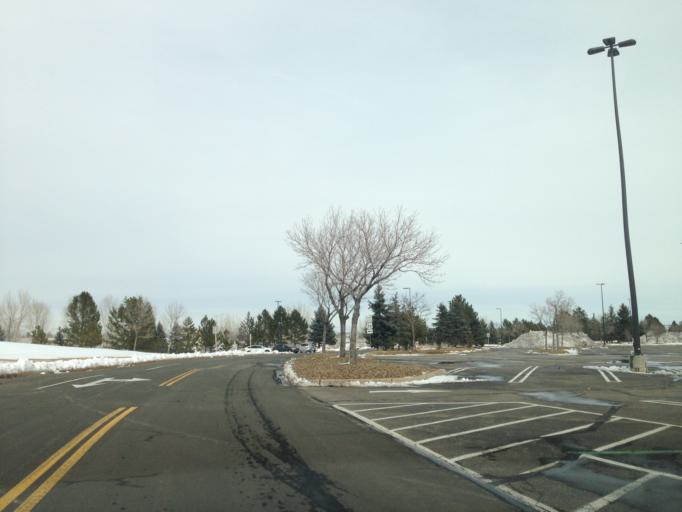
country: US
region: Colorado
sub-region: Boulder County
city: Superior
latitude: 39.9352
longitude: -105.1367
